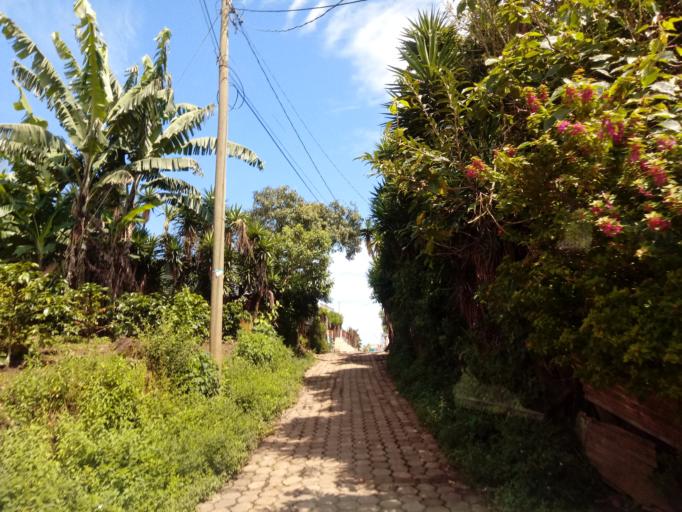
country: GT
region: Guatemala
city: Amatitlan
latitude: 14.4586
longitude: -90.6084
